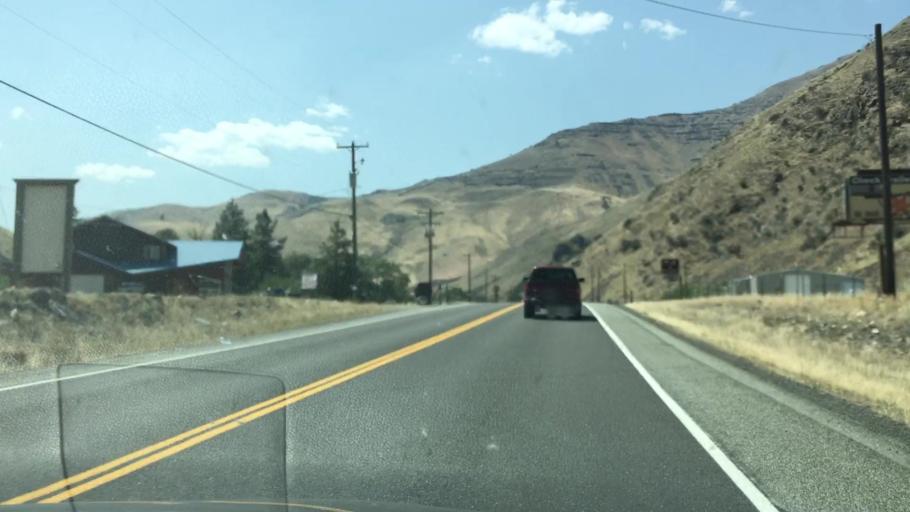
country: US
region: Idaho
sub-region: Valley County
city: McCall
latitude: 45.3971
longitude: -116.3341
